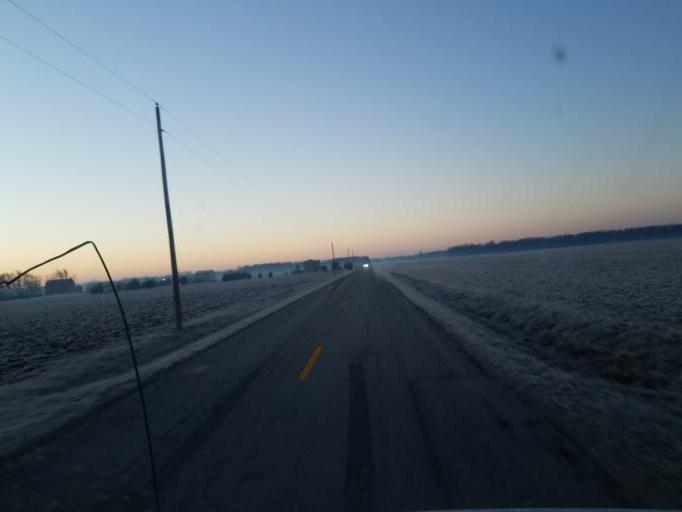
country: US
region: Ohio
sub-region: Marion County
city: Marion
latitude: 40.5680
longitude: -83.0196
